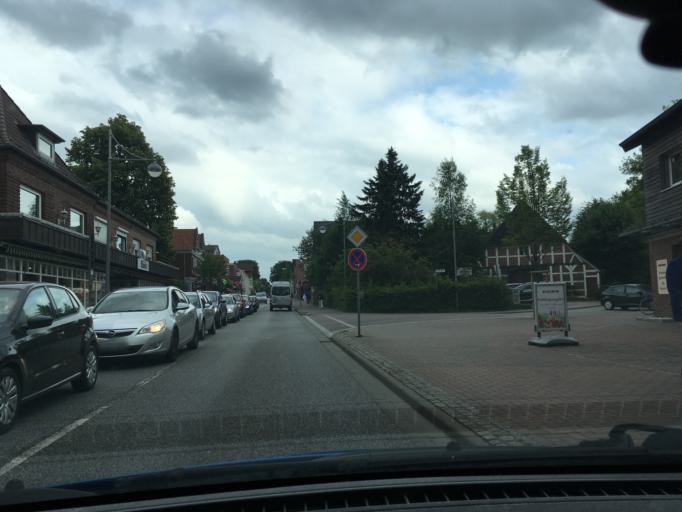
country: DE
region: Lower Saxony
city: Tostedt
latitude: 53.2807
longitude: 9.7127
